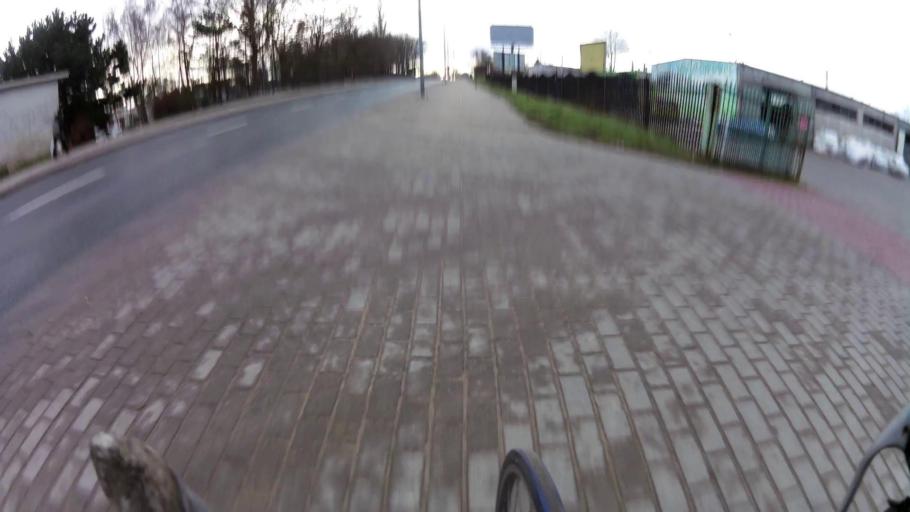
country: PL
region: West Pomeranian Voivodeship
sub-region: Koszalin
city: Koszalin
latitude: 54.1809
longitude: 16.1850
